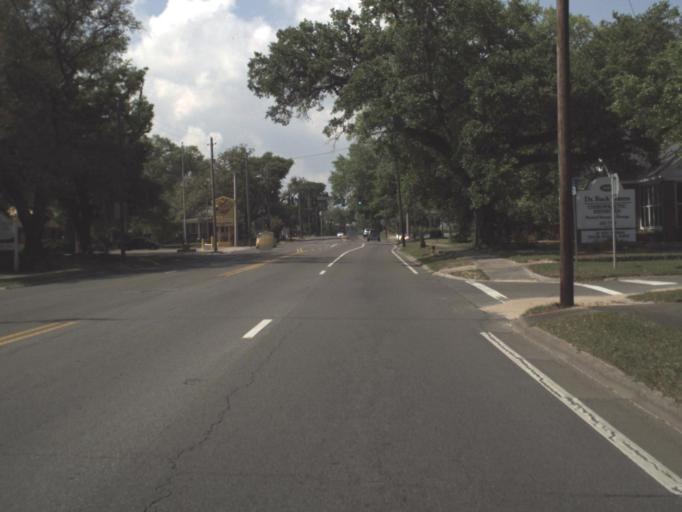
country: US
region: Florida
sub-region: Escambia County
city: Pensacola
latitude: 30.4285
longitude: -87.2083
